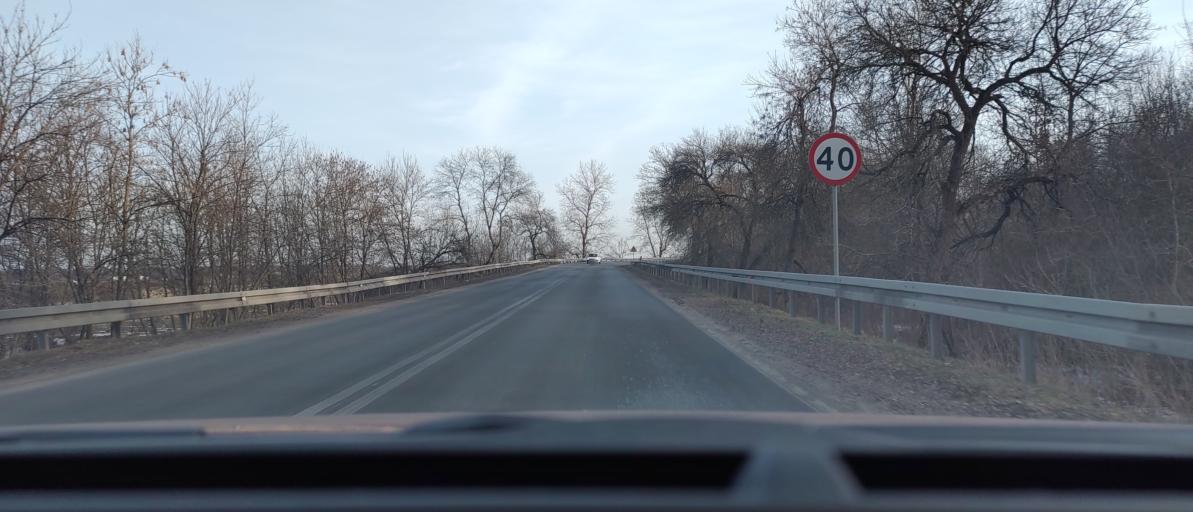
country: PL
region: Masovian Voivodeship
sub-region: Powiat bialobrzeski
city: Bialobrzegi
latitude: 51.6610
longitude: 20.9517
